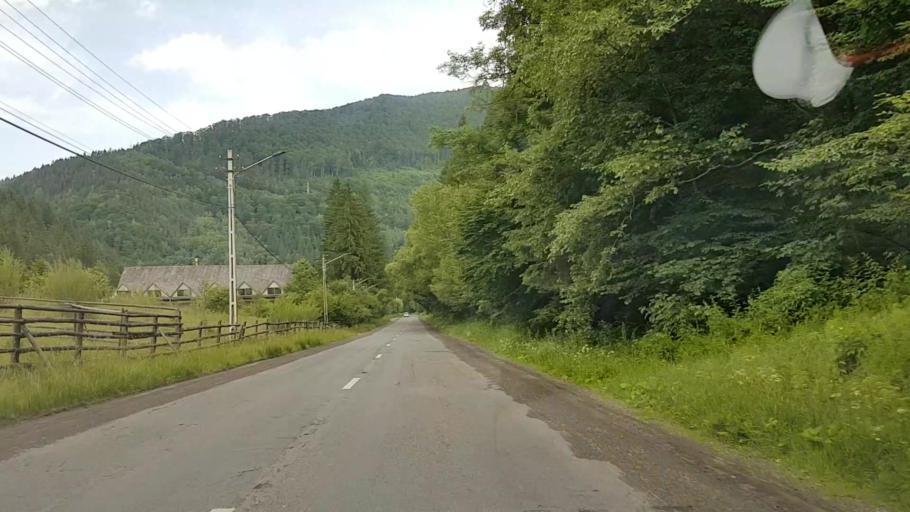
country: RO
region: Neamt
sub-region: Comuna Bicaz
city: Dodeni
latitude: 46.9375
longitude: 26.0893
